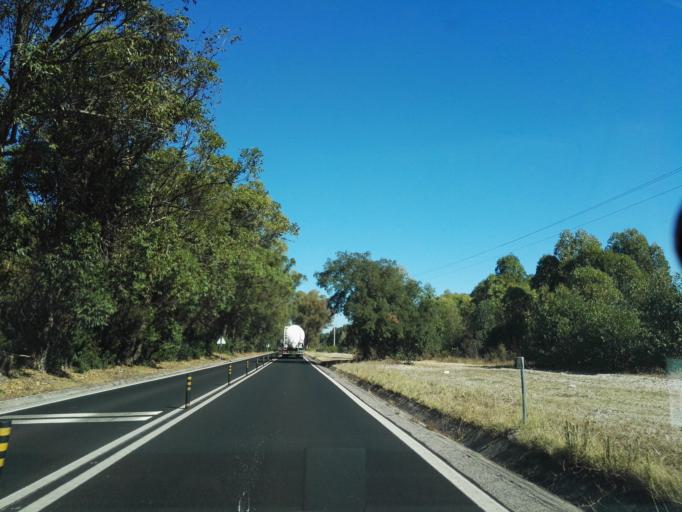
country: PT
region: Setubal
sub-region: Alcochete
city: Alcochete
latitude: 38.7857
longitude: -8.8807
